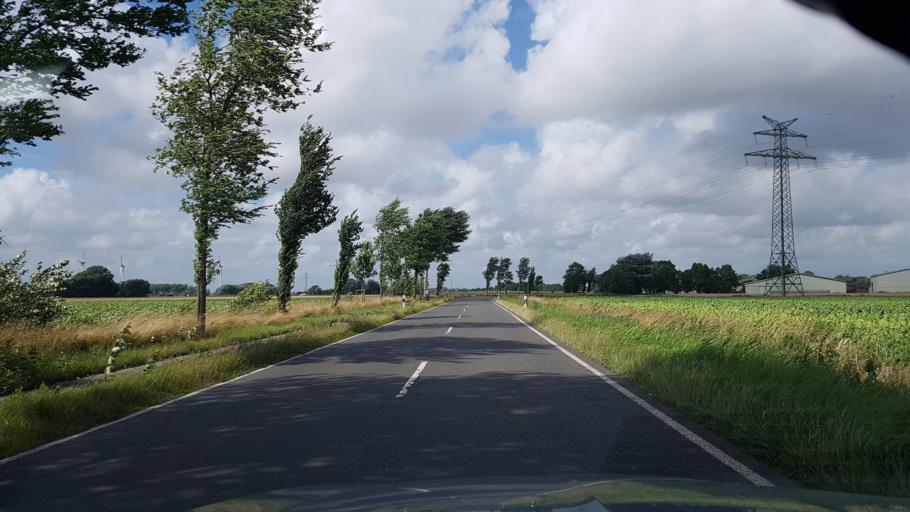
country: DE
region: Schleswig-Holstein
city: Reinsbuttel
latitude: 54.1913
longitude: 8.9024
